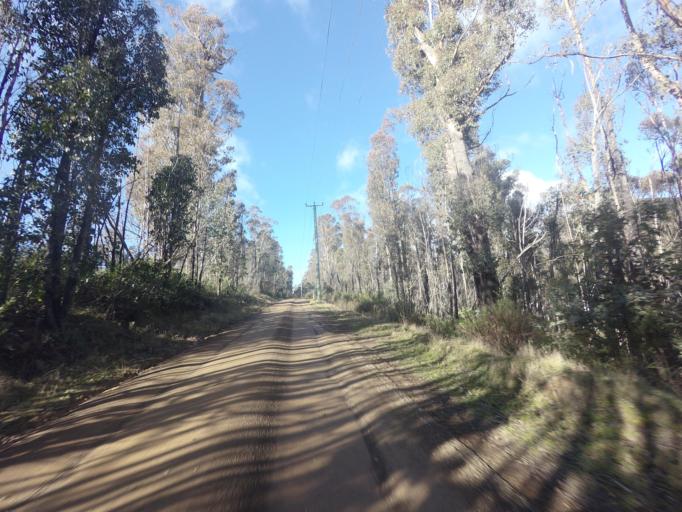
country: AU
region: Tasmania
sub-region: Derwent Valley
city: New Norfolk
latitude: -42.8422
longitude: 147.1389
